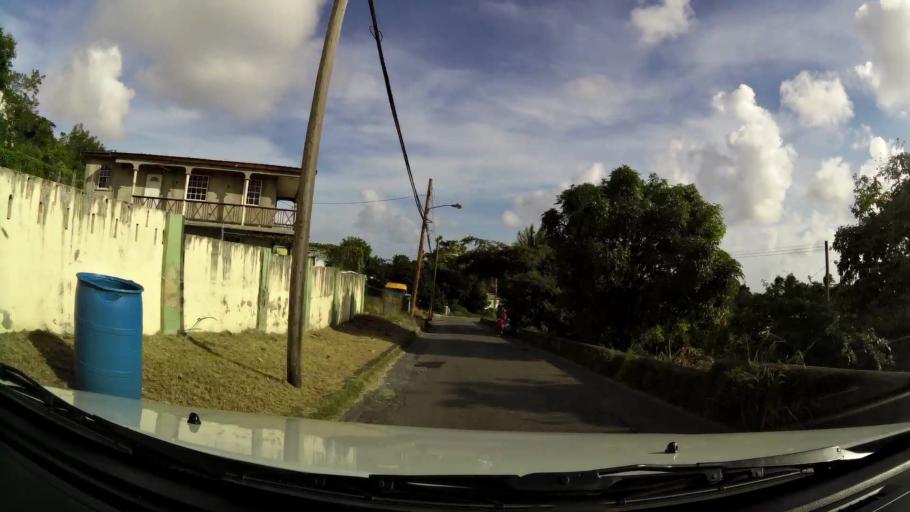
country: BB
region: Saint Michael
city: Bridgetown
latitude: 13.0872
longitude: -59.5888
